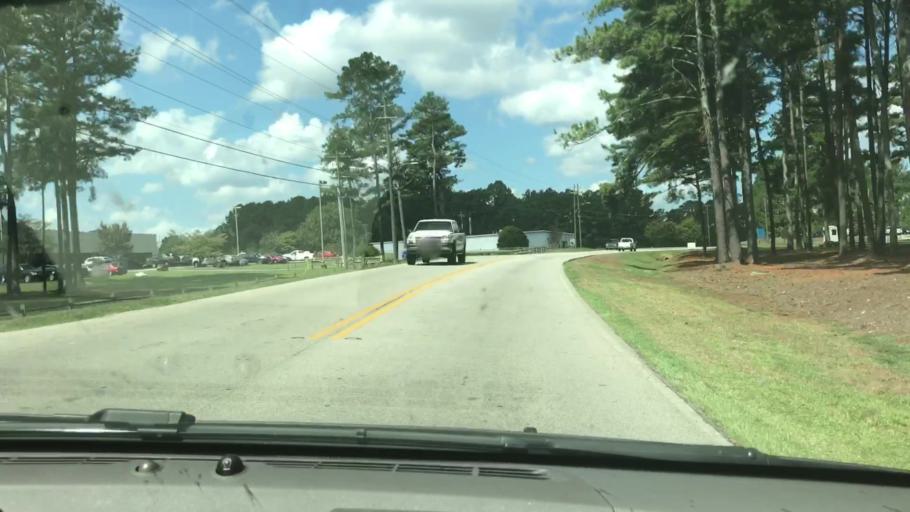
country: US
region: Georgia
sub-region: Troup County
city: La Grange
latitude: 33.0127
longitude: -85.0630
